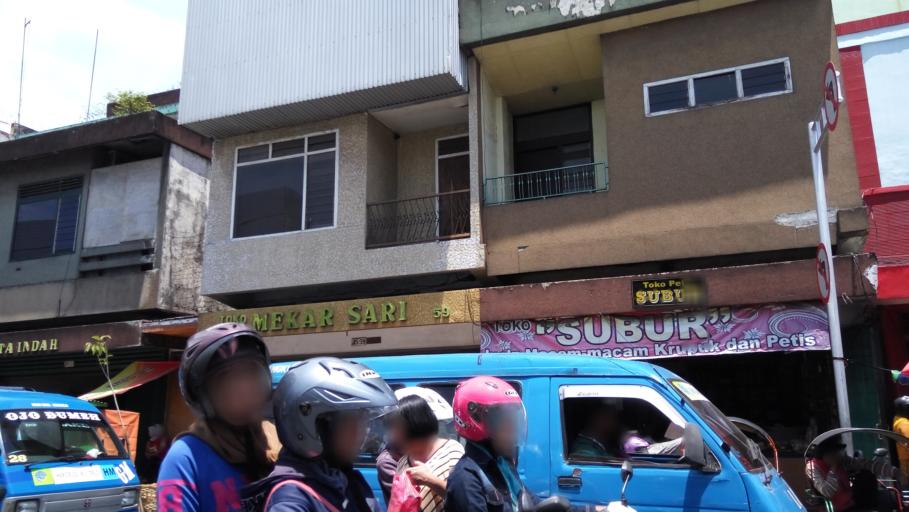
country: ID
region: East Java
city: Malang
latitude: -7.9886
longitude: 112.6333
